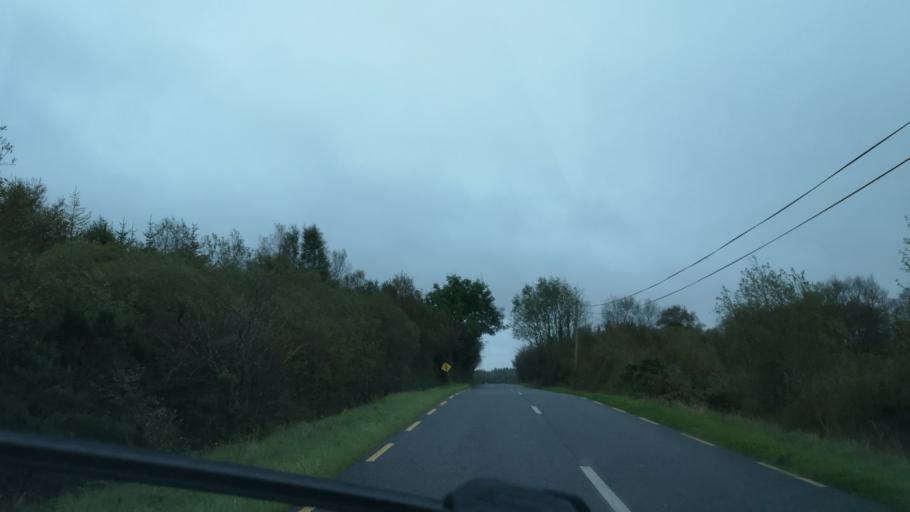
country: IE
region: Connaught
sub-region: Maigh Eo
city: Ballyhaunis
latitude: 53.8020
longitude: -8.6915
